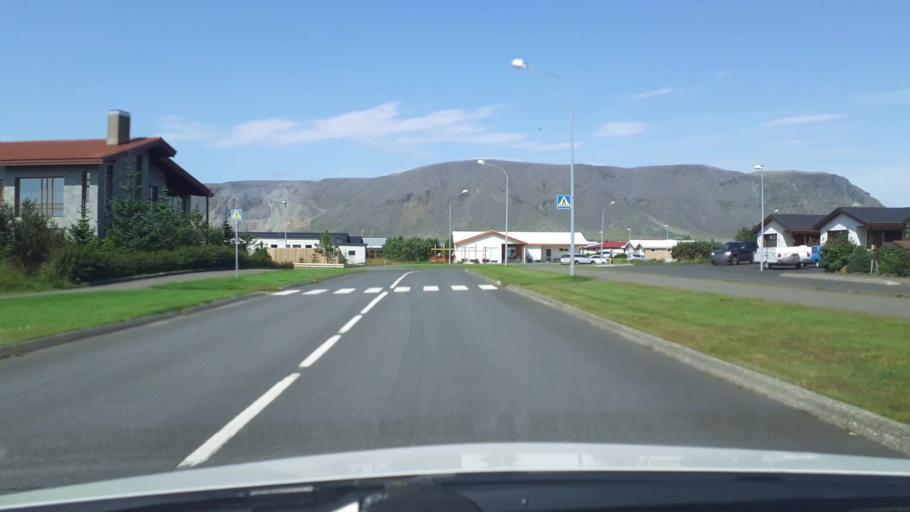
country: IS
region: South
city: Selfoss
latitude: 63.9333
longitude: -21.0201
